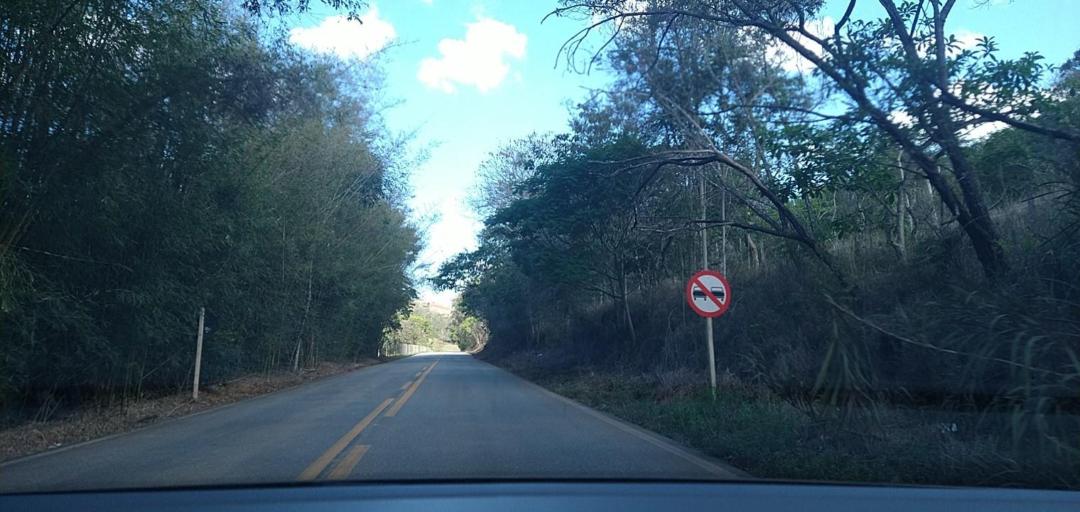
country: BR
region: Minas Gerais
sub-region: Alvinopolis
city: Alvinopolis
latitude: -20.0291
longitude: -43.0515
